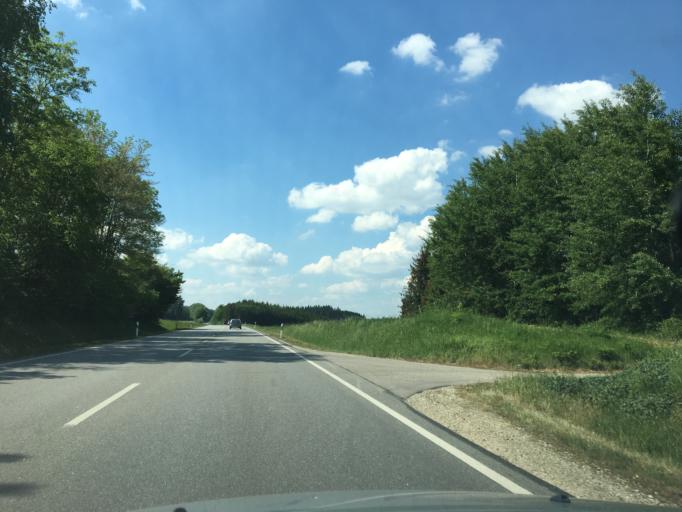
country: DE
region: Bavaria
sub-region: Lower Bavaria
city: Geisenhausen
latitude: 48.4956
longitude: 12.2263
